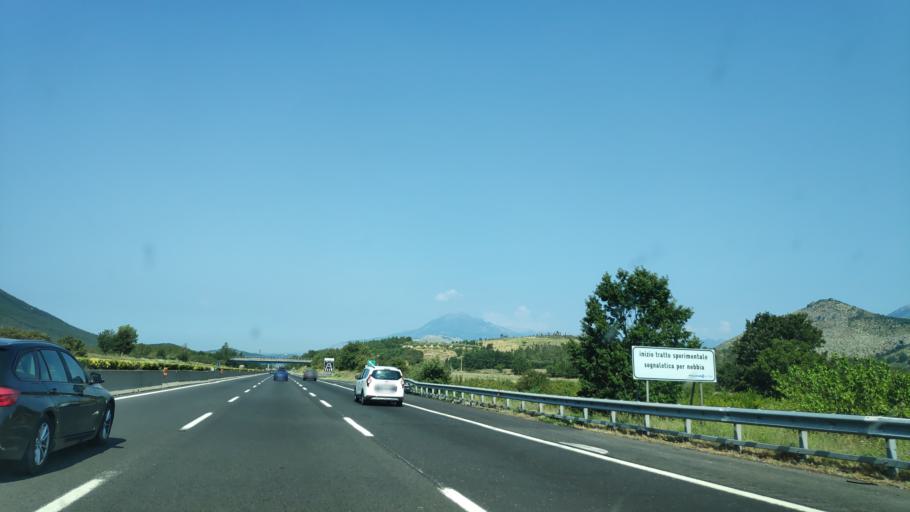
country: IT
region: Campania
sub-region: Provincia di Caserta
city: San Pietro Infine
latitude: 41.4123
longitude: 13.9505
